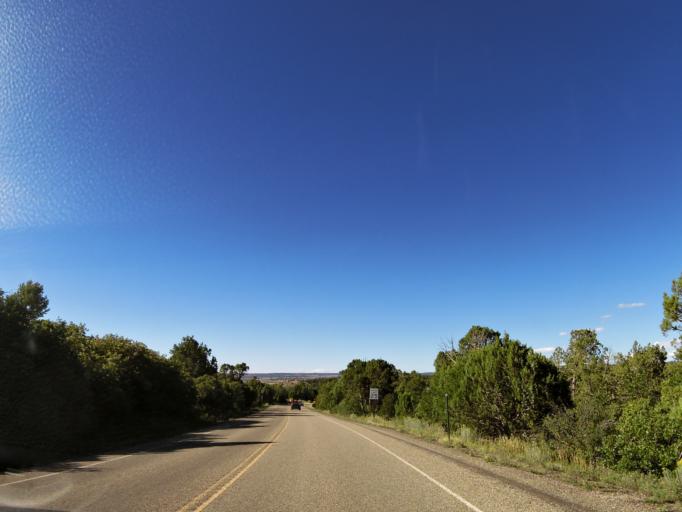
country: US
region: Colorado
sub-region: Montezuma County
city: Mancos
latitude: 37.3369
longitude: -108.4116
